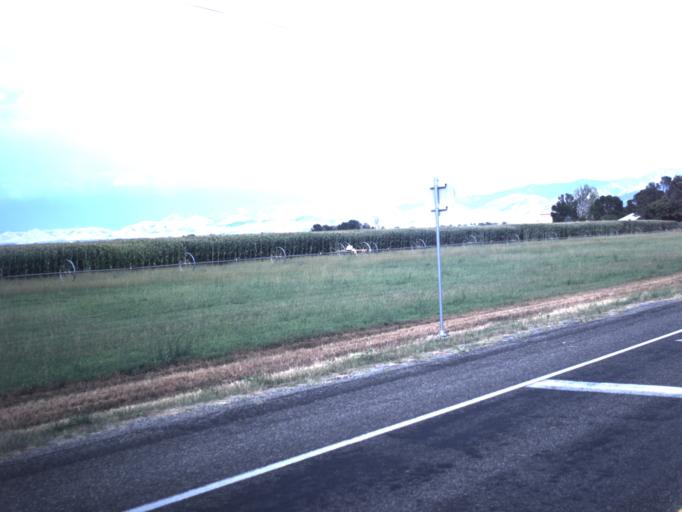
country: US
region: Utah
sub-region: Cache County
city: Lewiston
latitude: 41.9754
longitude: -111.9515
